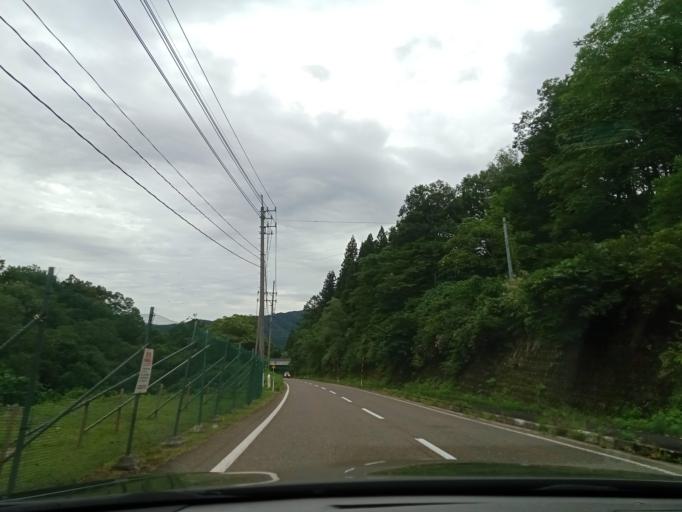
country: JP
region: Niigata
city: Arai
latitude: 36.8792
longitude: 138.1943
